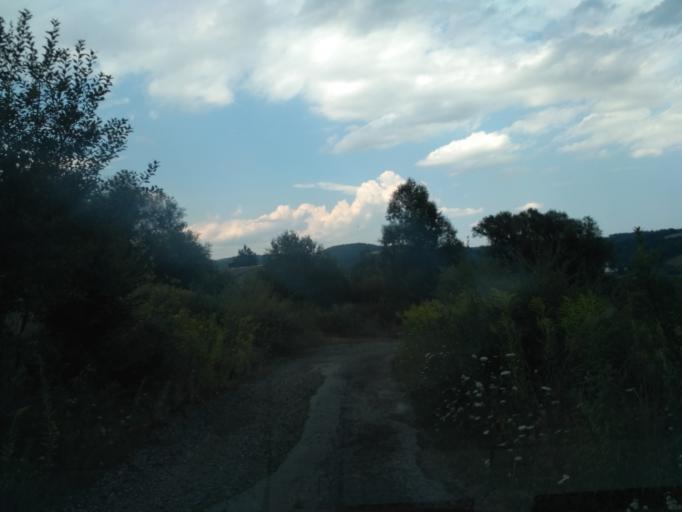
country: SK
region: Presovsky
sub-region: Okres Presov
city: Presov
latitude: 48.9233
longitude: 21.1830
